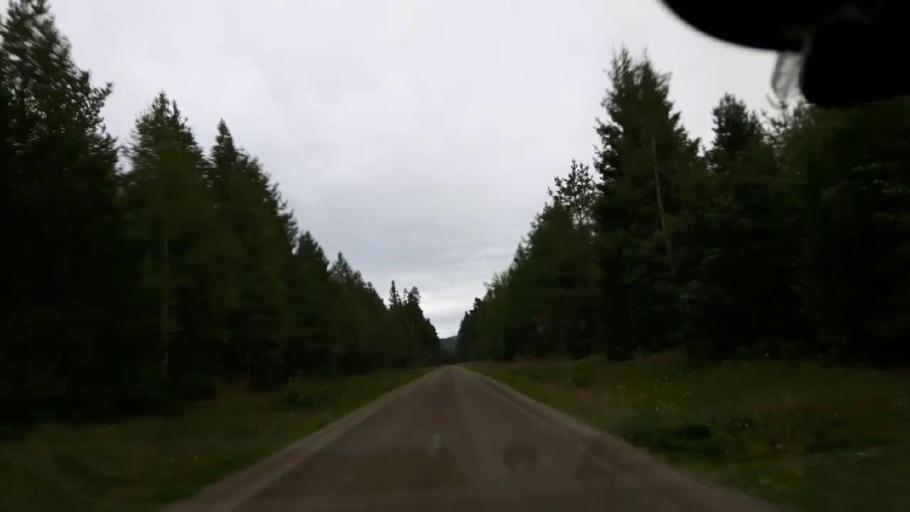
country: SE
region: Jaemtland
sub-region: Braecke Kommun
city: Braecke
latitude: 62.9380
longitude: 15.4592
